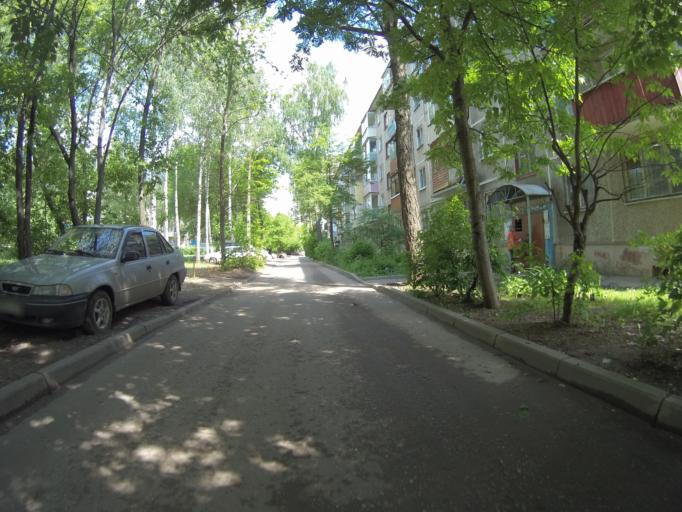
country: RU
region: Vladimir
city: Vladimir
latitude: 56.1273
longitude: 40.3520
